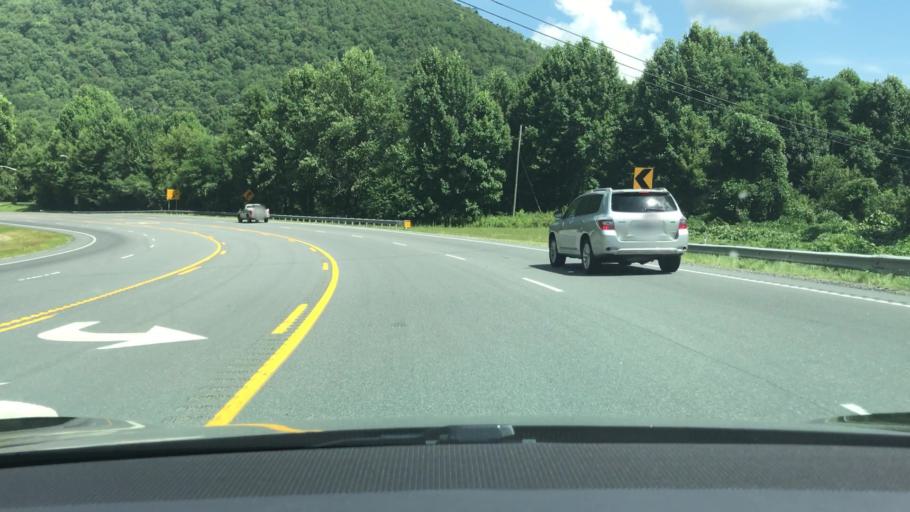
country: US
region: North Carolina
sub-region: Macon County
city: Franklin
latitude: 35.2630
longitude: -83.2983
